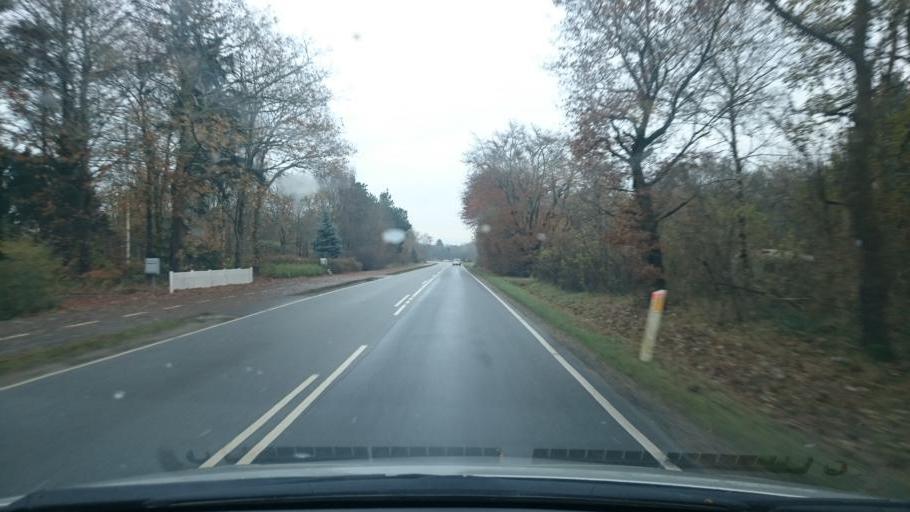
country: DK
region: South Denmark
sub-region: Esbjerg Kommune
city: Ribe
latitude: 55.3339
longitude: 8.7943
